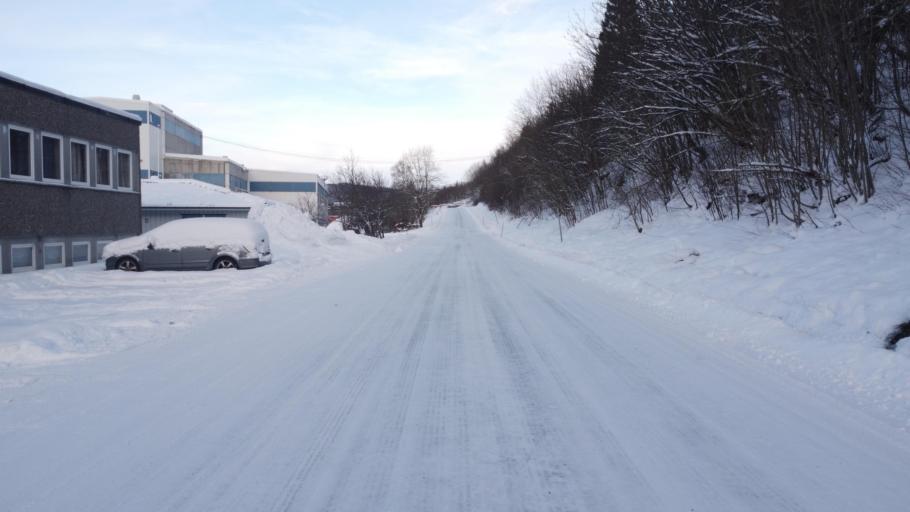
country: NO
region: Nordland
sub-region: Rana
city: Mo i Rana
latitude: 66.3219
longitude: 14.1546
